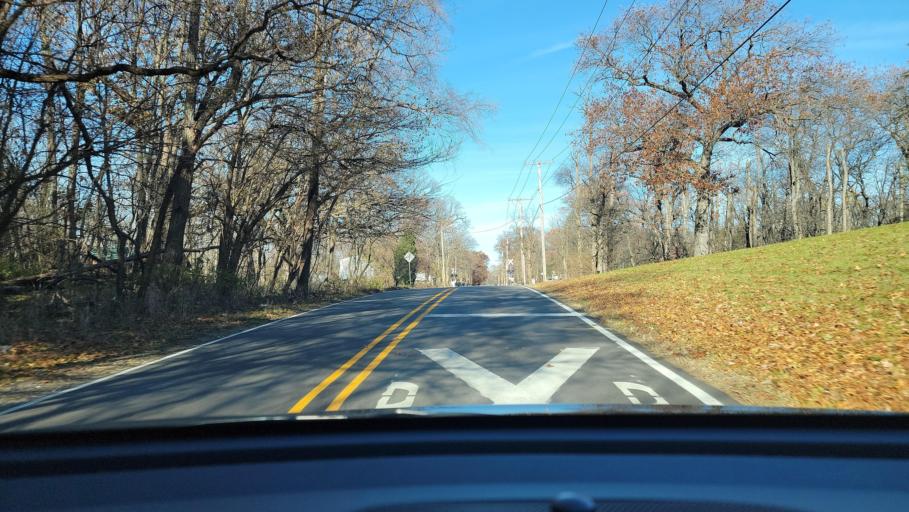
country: US
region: Indiana
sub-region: Porter County
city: Portage
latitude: 41.5840
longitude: -87.1978
